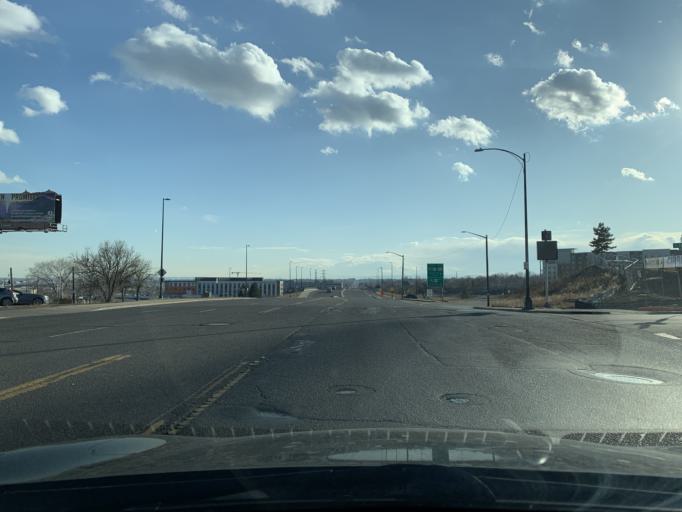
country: US
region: Colorado
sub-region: Jefferson County
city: Edgewater
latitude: 39.7429
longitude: -105.0253
